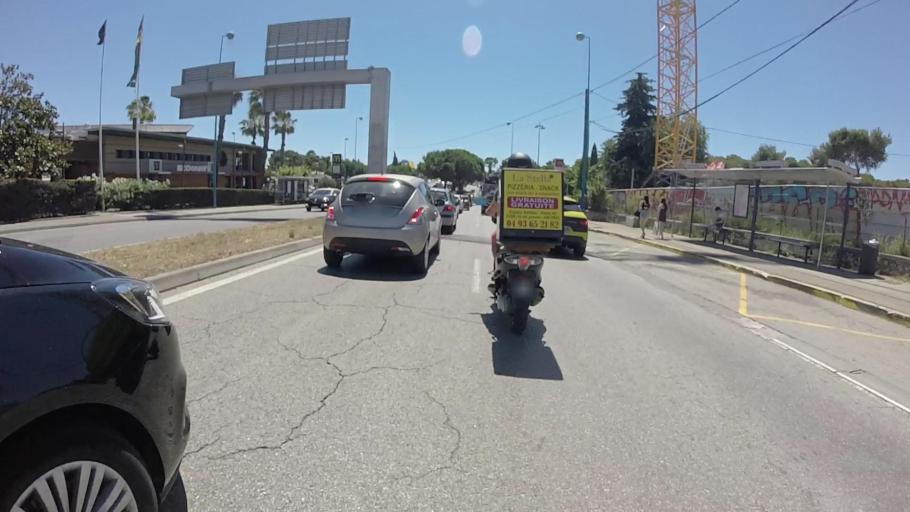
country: FR
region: Provence-Alpes-Cote d'Azur
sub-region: Departement des Alpes-Maritimes
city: Biot
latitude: 43.5999
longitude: 7.0858
